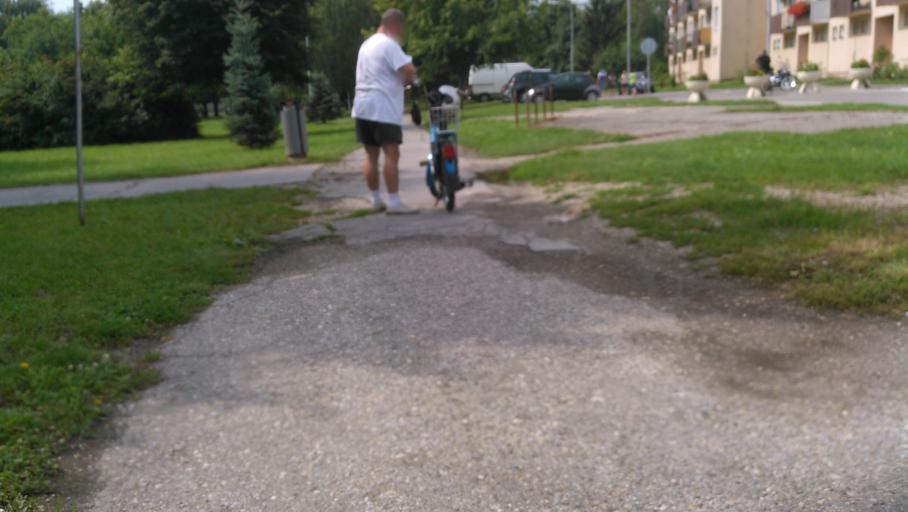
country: SK
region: Nitriansky
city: Kolarovo
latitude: 47.9166
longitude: 17.9955
